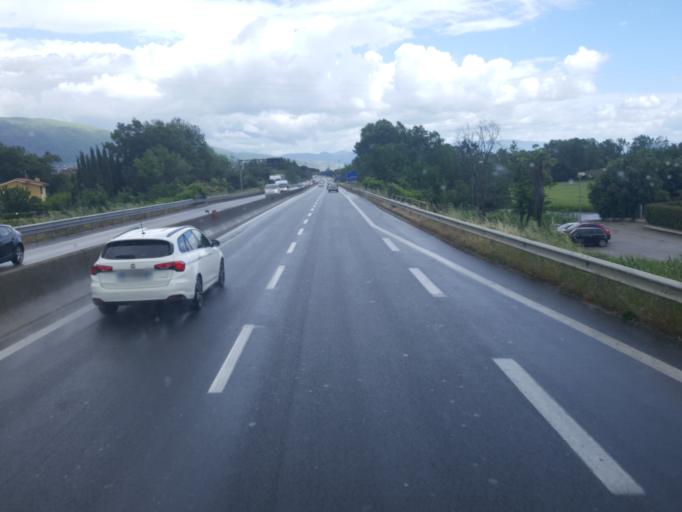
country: IT
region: Umbria
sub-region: Provincia di Perugia
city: Bastia umbra
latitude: 43.0652
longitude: 12.5398
